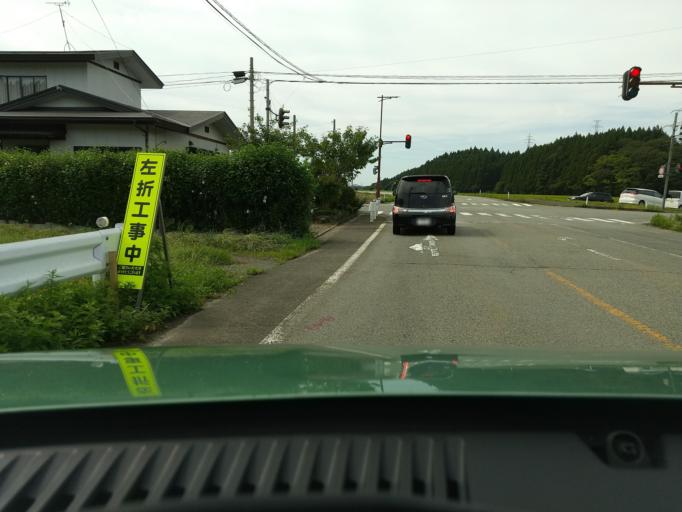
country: JP
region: Akita
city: Akita Shi
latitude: 39.7911
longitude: 140.1119
